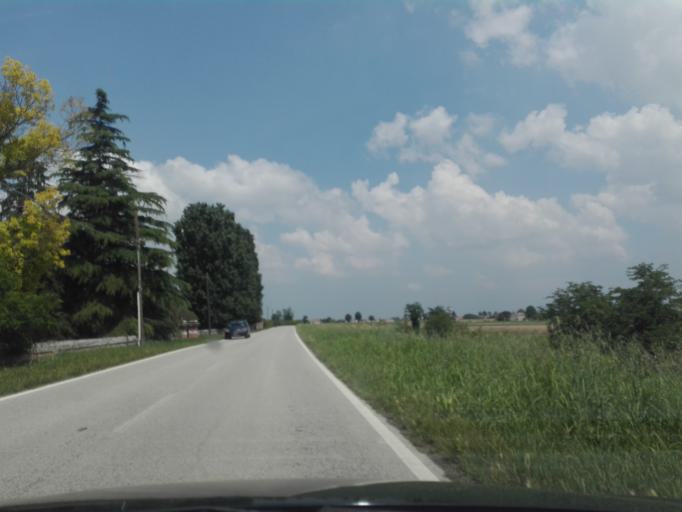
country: IT
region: Veneto
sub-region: Provincia di Rovigo
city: Adria
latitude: 45.0584
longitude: 12.0016
